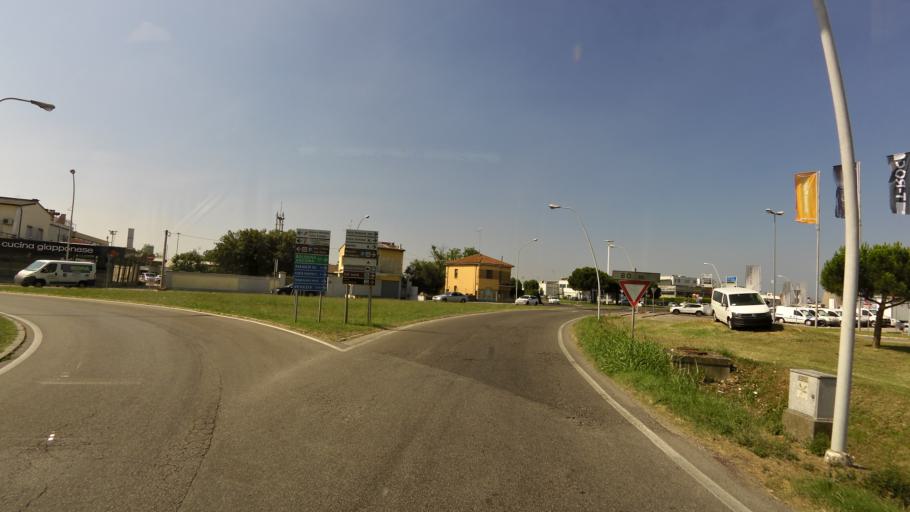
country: IT
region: Emilia-Romagna
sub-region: Provincia di Ravenna
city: Ravenna
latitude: 44.4240
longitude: 12.2278
